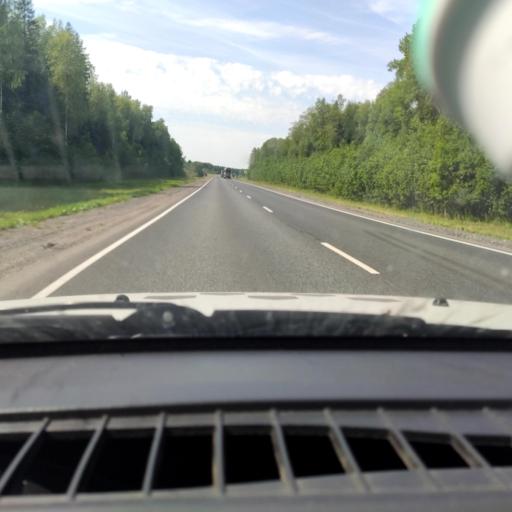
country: RU
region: Kirov
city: Kostino
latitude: 58.7119
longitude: 53.6903
